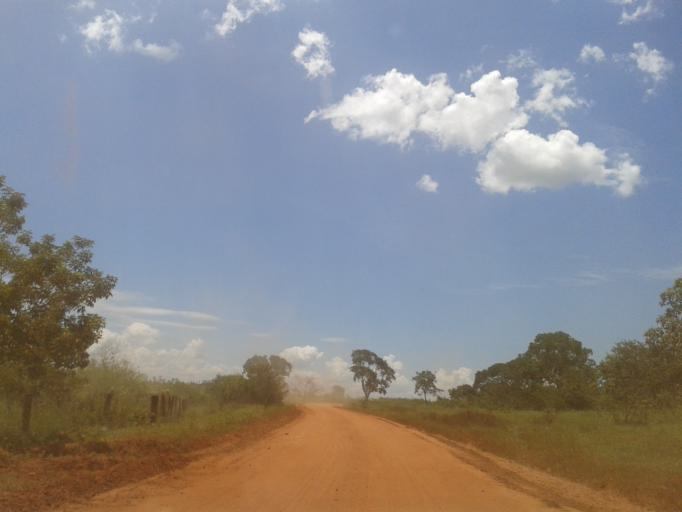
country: BR
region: Minas Gerais
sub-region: Santa Vitoria
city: Santa Vitoria
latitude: -19.1761
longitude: -50.4052
